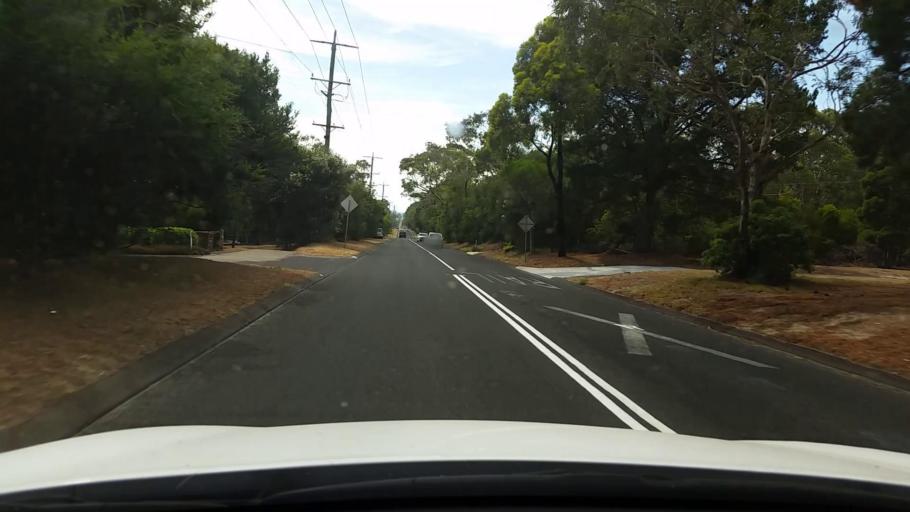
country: AU
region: Victoria
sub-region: Mornington Peninsula
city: Tyabb
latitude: -38.2385
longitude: 145.1820
